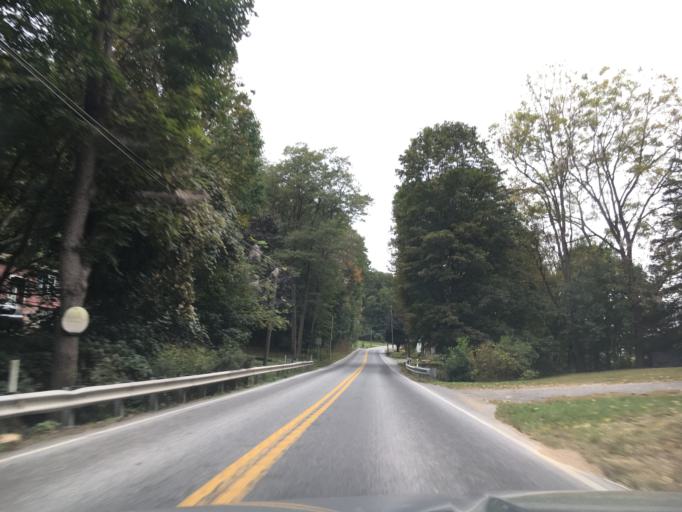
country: US
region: Pennsylvania
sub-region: Lancaster County
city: Quarryville
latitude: 39.8858
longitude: -76.1925
